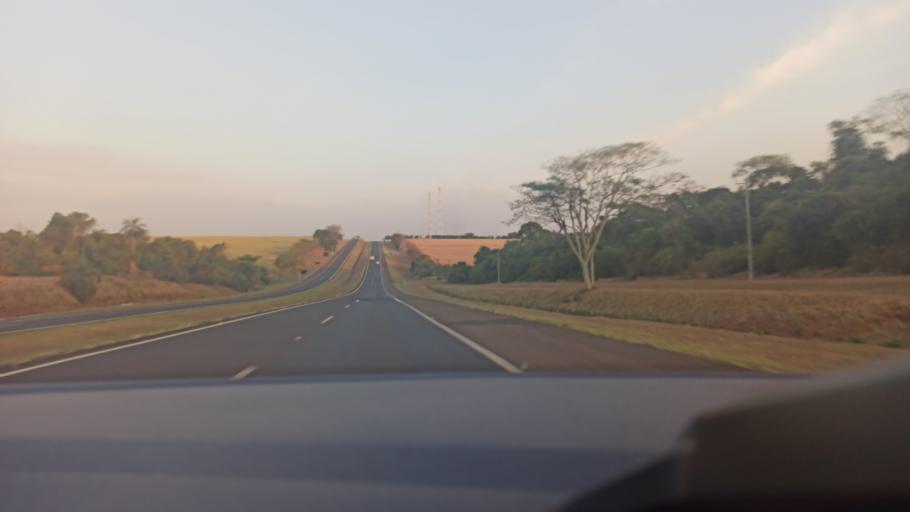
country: BR
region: Sao Paulo
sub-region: Taquaritinga
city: Taquaritinga
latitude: -21.4175
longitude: -48.6828
